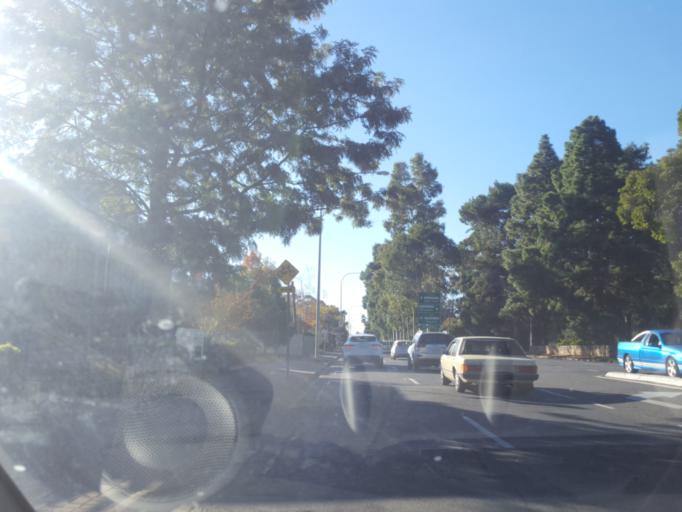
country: AU
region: South Australia
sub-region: Unley
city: Fullarton
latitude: -34.9435
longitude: 138.6248
